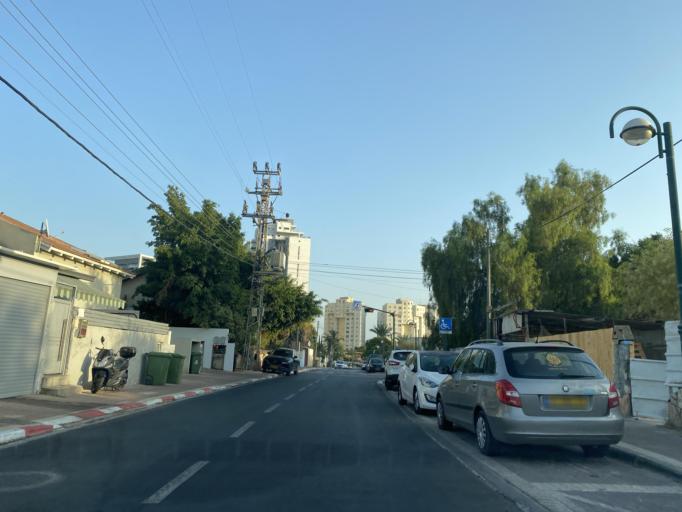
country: IL
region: Tel Aviv
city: Ramat HaSharon
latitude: 32.1343
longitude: 34.8624
